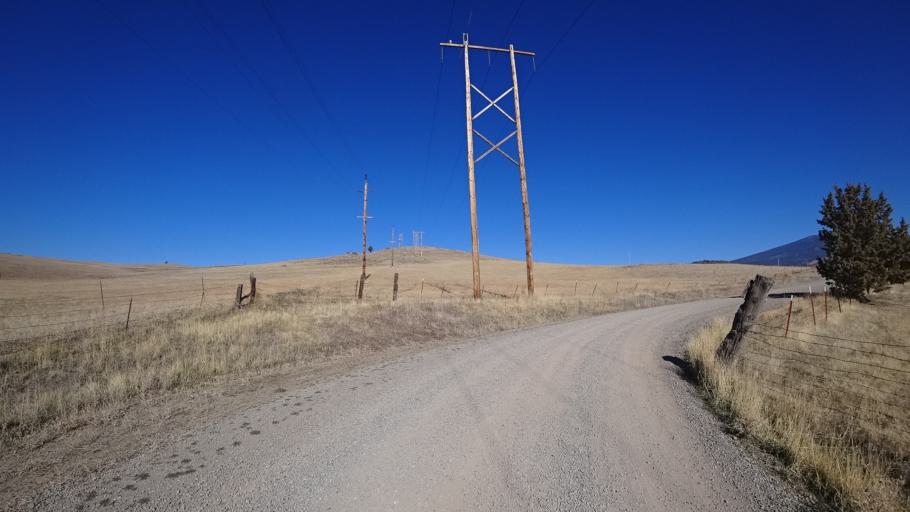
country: US
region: California
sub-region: Siskiyou County
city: Montague
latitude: 41.7624
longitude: -122.3593
